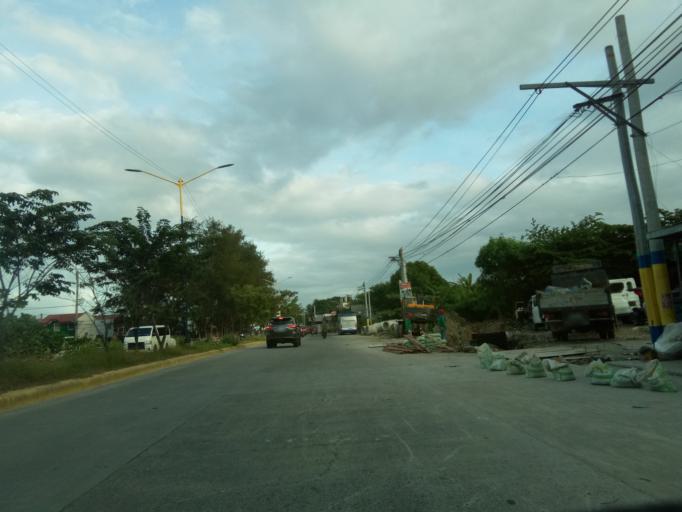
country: PH
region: Calabarzon
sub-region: Province of Cavite
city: Imus
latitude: 14.3872
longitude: 120.9729
